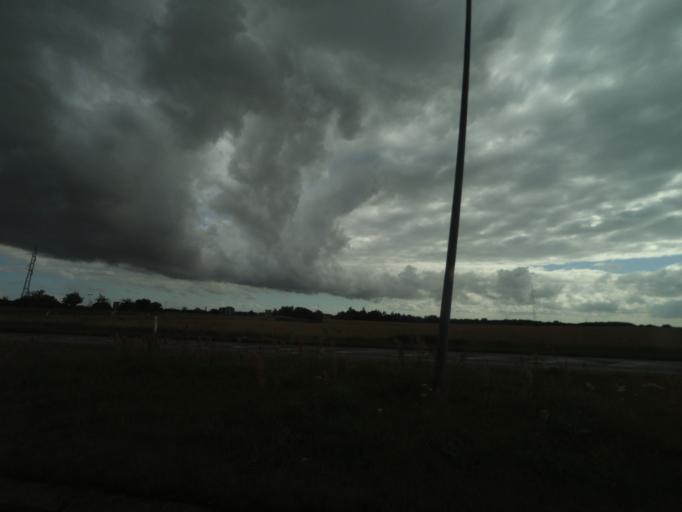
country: DK
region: South Denmark
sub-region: Middelfart Kommune
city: Ejby
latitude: 55.4567
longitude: 9.9490
